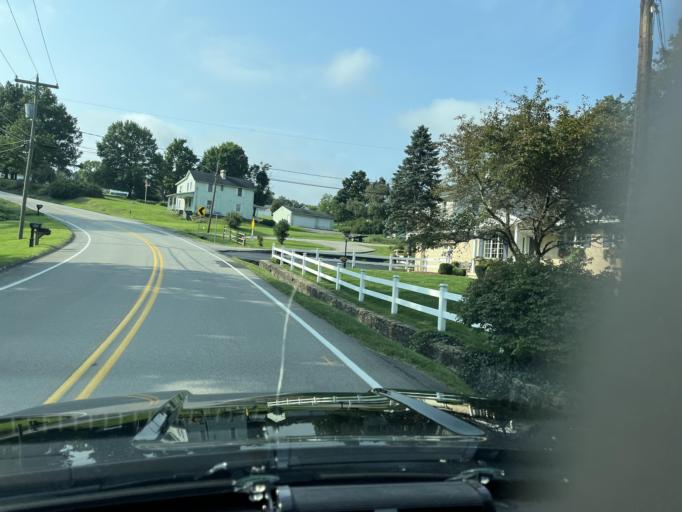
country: US
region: Pennsylvania
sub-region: Fayette County
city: Hopwood
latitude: 39.8617
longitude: -79.7109
